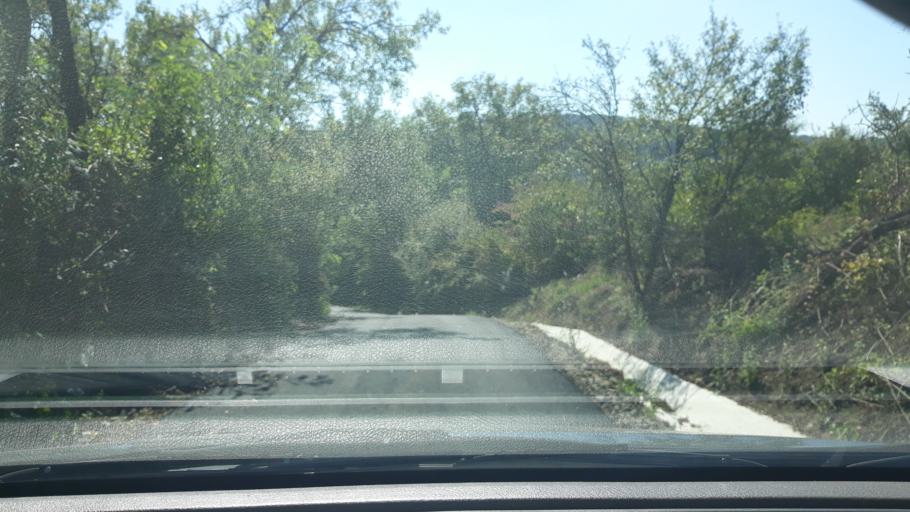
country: RO
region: Salaj
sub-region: Comuna Dobrin
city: Dobrin
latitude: 47.2936
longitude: 23.0844
